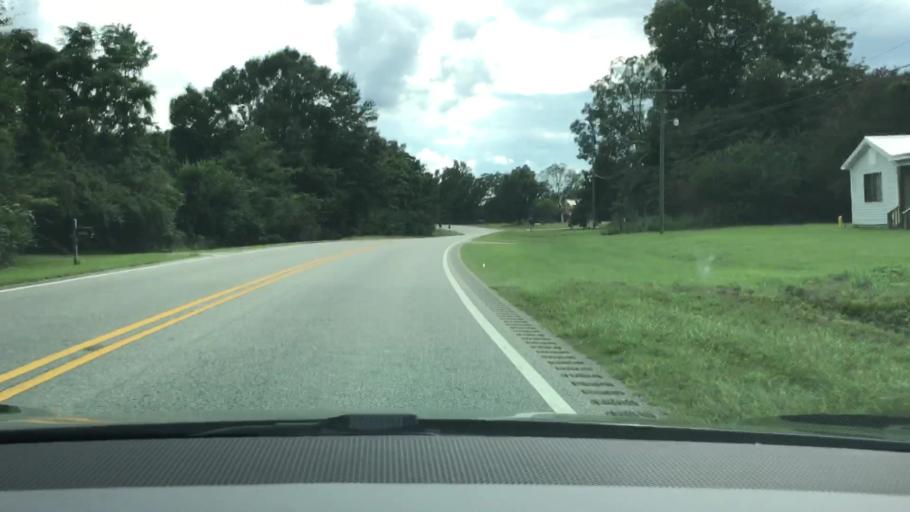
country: US
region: Alabama
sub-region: Pike County
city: Troy
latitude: 31.6088
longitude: -85.9965
